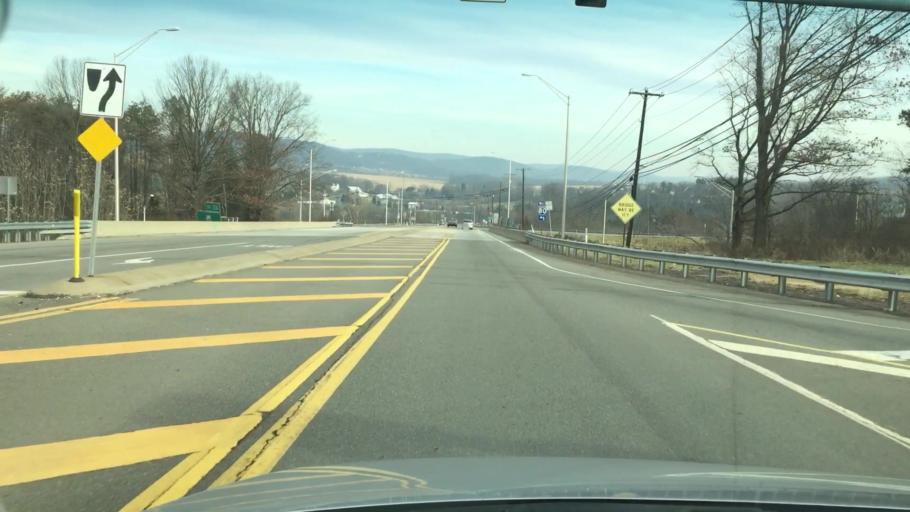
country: US
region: Pennsylvania
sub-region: Columbia County
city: Light Street
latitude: 41.0262
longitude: -76.4265
